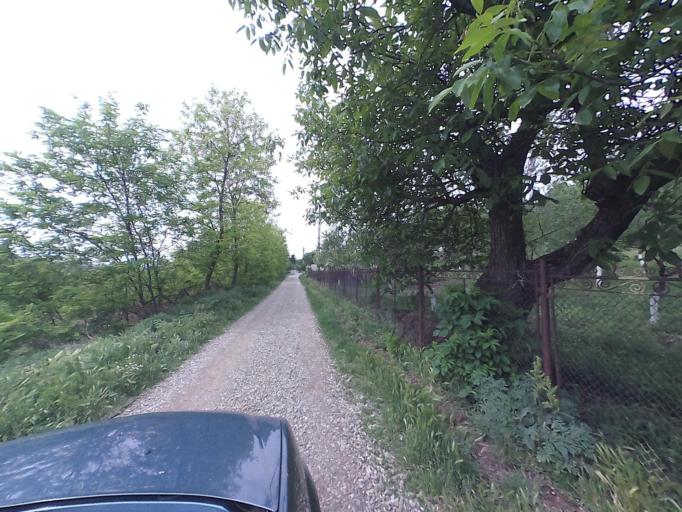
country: RO
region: Neamt
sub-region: Comuna Dulcesti
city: Dulcesti
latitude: 46.9549
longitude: 26.7995
